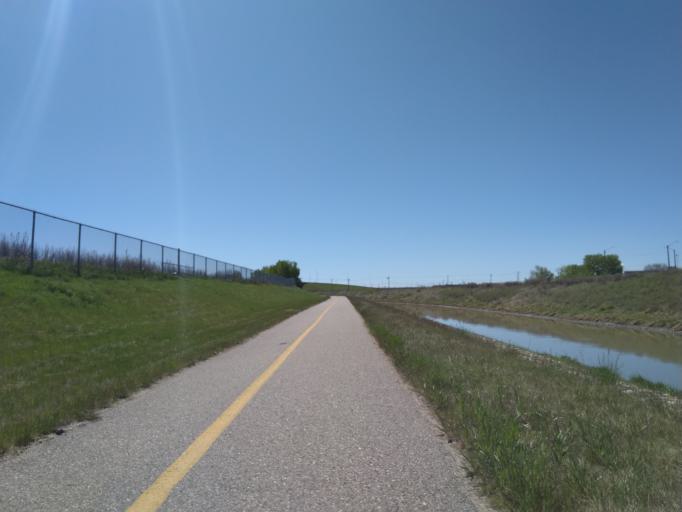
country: CA
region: Alberta
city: Calgary
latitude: 50.9688
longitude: -113.9860
